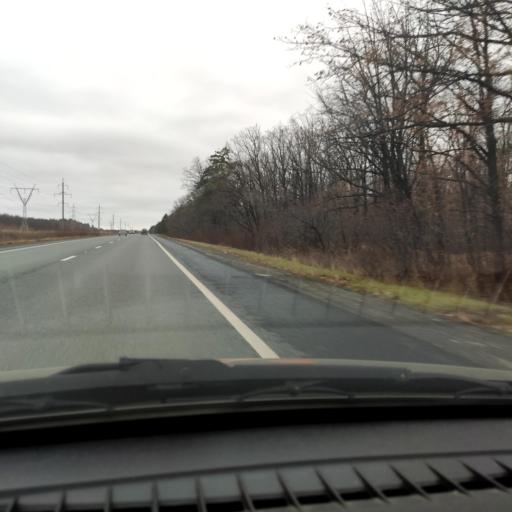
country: RU
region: Samara
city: Bogatyr'
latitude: 53.5015
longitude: 49.9500
